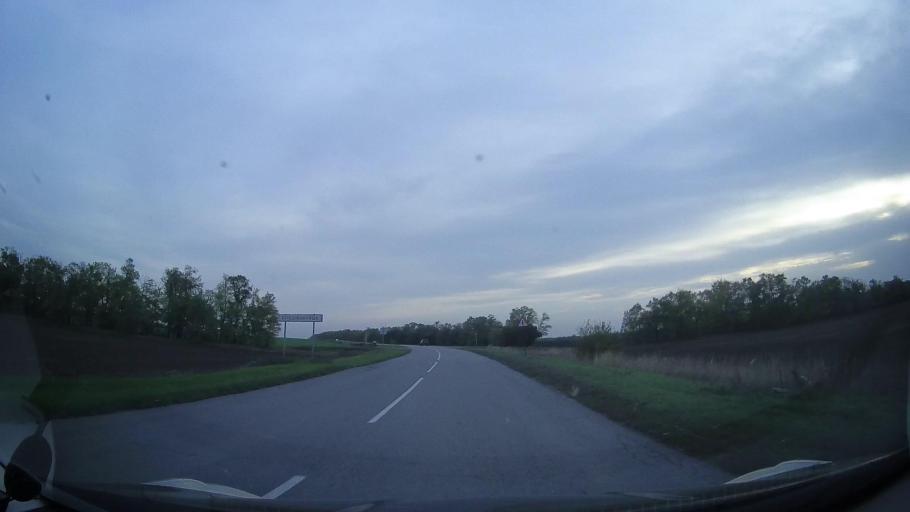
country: RU
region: Rostov
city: Kirovskaya
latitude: 47.0273
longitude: 39.9792
